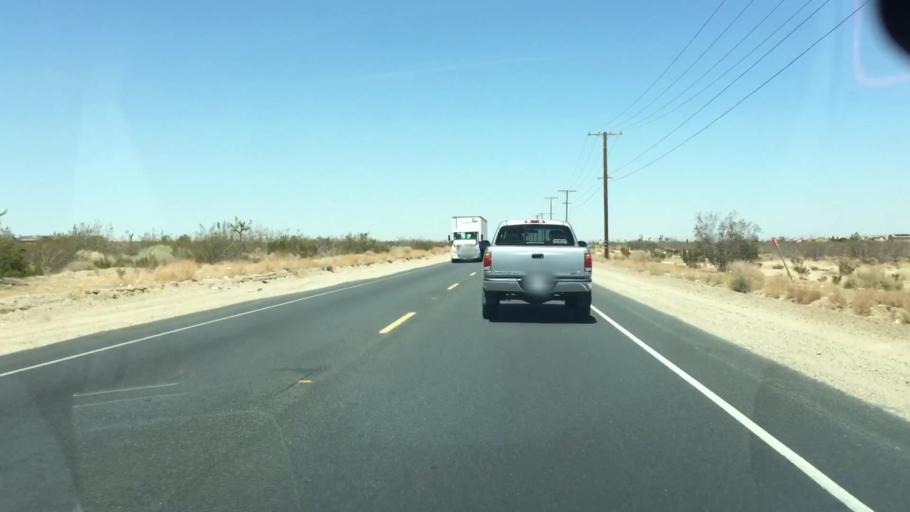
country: US
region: California
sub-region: San Bernardino County
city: Mountain View Acres
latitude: 34.4759
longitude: -117.3995
